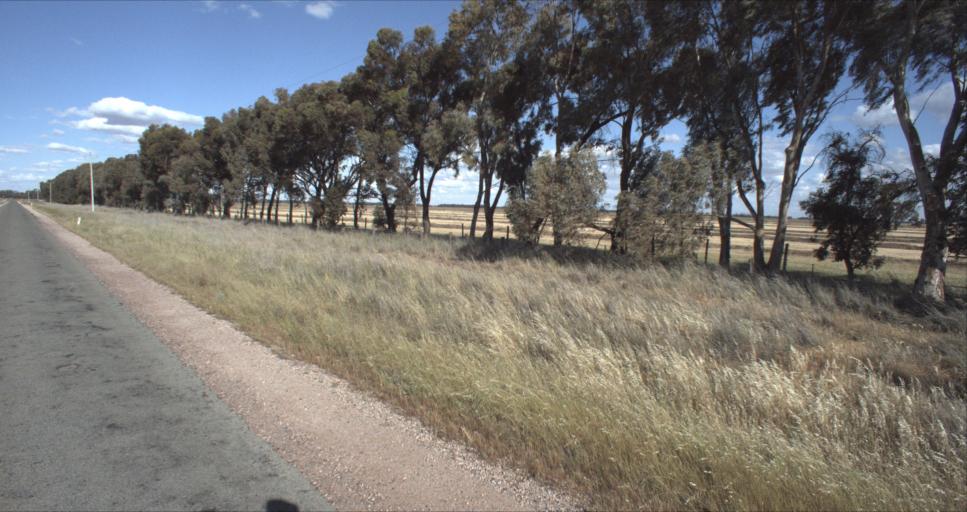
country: AU
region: New South Wales
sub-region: Leeton
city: Leeton
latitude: -34.4587
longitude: 146.2641
